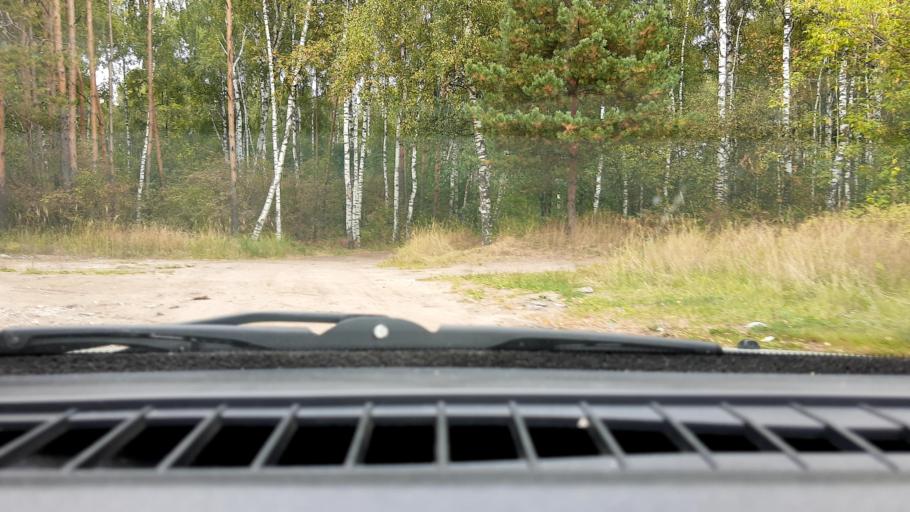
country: RU
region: Nizjnij Novgorod
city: Gorbatovka
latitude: 56.3114
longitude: 43.6993
